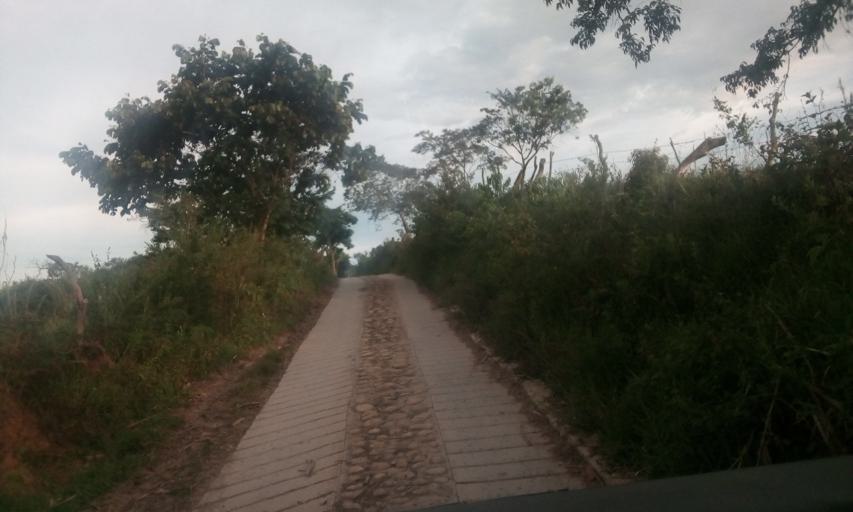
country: CO
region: Boyaca
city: Santana
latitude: 6.0193
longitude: -73.5126
